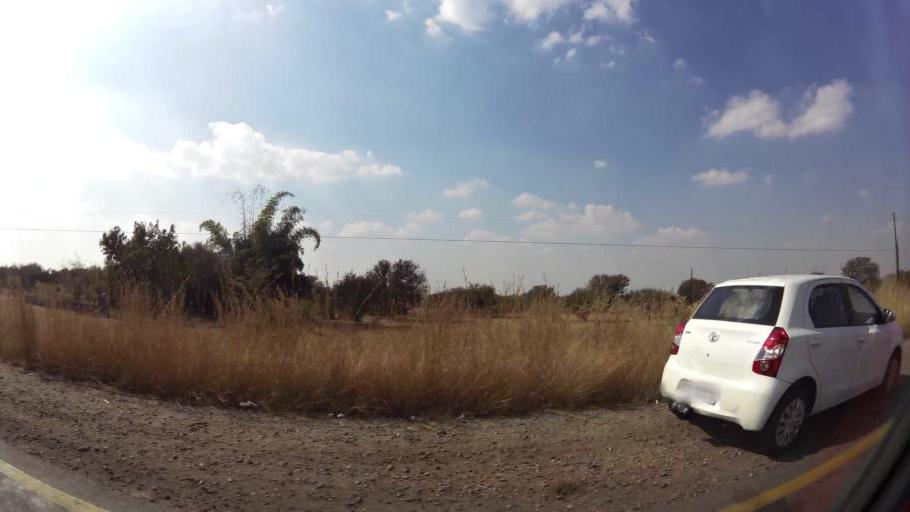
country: ZA
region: North-West
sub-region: Bojanala Platinum District Municipality
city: Rustenburg
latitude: -25.5245
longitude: 27.1097
